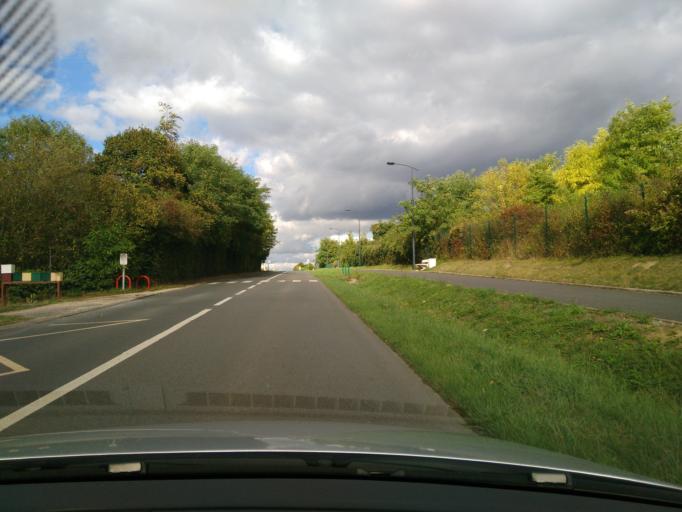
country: FR
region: Ile-de-France
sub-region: Departement de Seine-et-Marne
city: Villenoy
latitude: 48.9367
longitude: 2.8701
